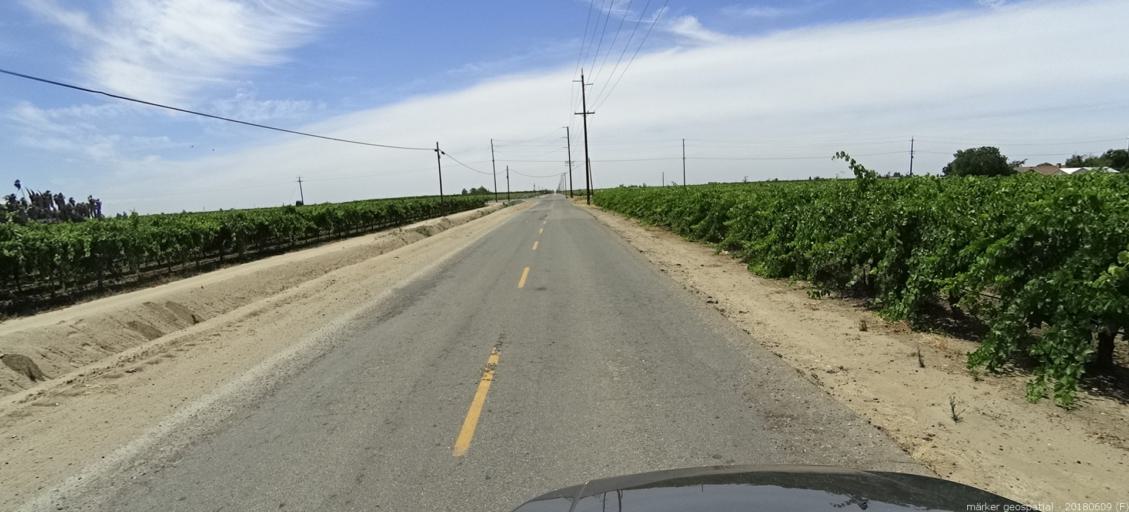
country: US
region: California
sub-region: Madera County
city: Parkwood
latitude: 36.9094
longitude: -120.0539
